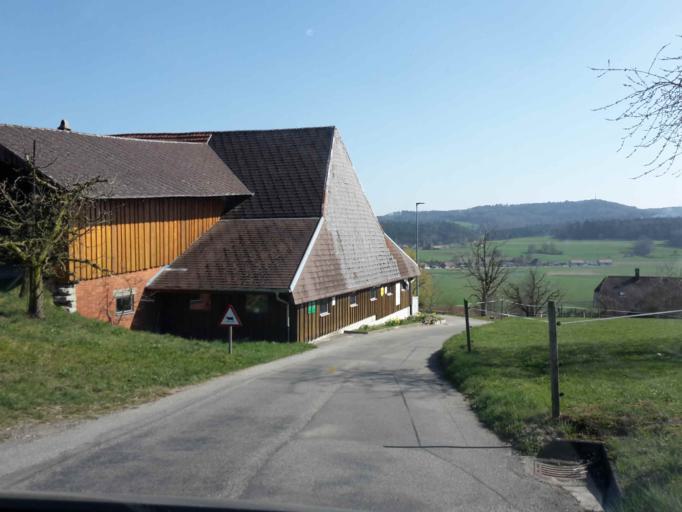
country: CH
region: Bern
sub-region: Oberaargau
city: Herzogenbuchsee
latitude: 47.1926
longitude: 7.7452
